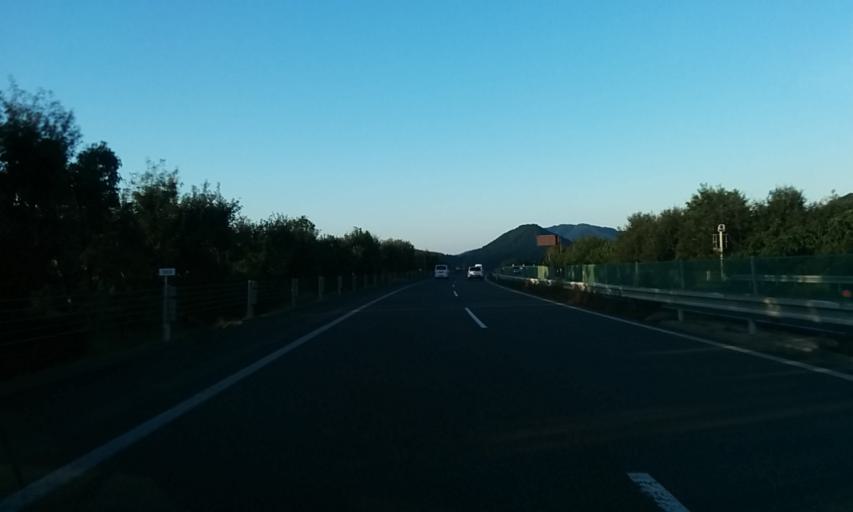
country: JP
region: Kyoto
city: Fukuchiyama
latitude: 35.1683
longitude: 135.1191
